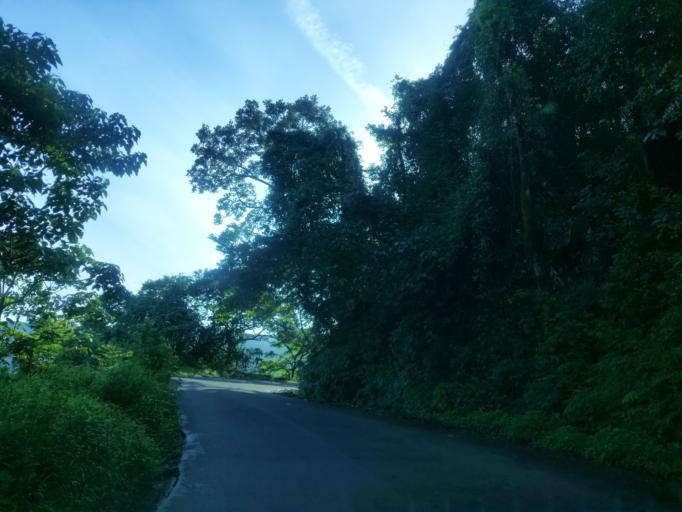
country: IN
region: Maharashtra
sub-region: Sindhudurg
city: Savantvadi
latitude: 15.9362
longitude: 73.9729
